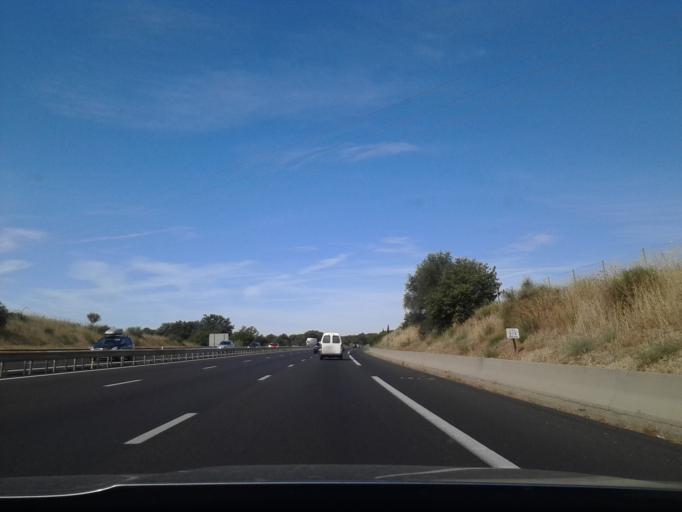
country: FR
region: Languedoc-Roussillon
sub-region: Departement de l'Herault
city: Montblanc
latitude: 43.3644
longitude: 3.3814
